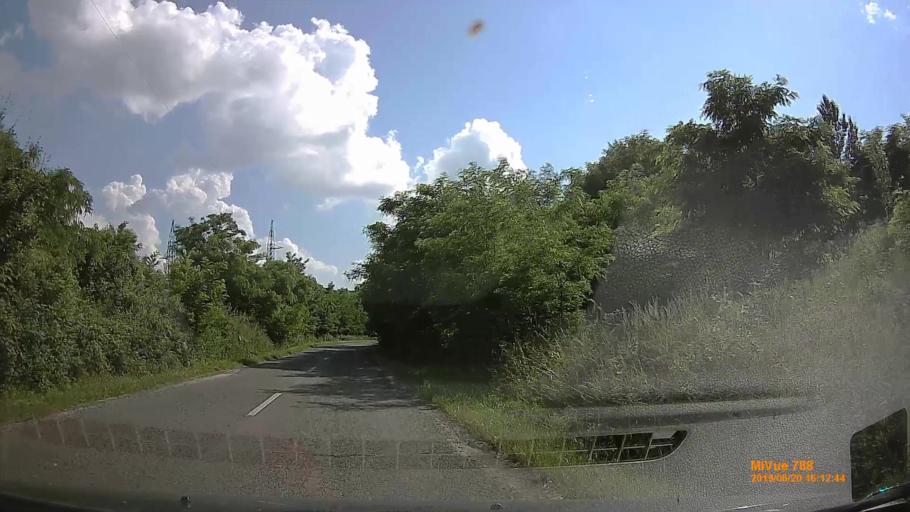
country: HU
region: Baranya
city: Pellerd
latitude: 46.0996
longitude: 18.0931
